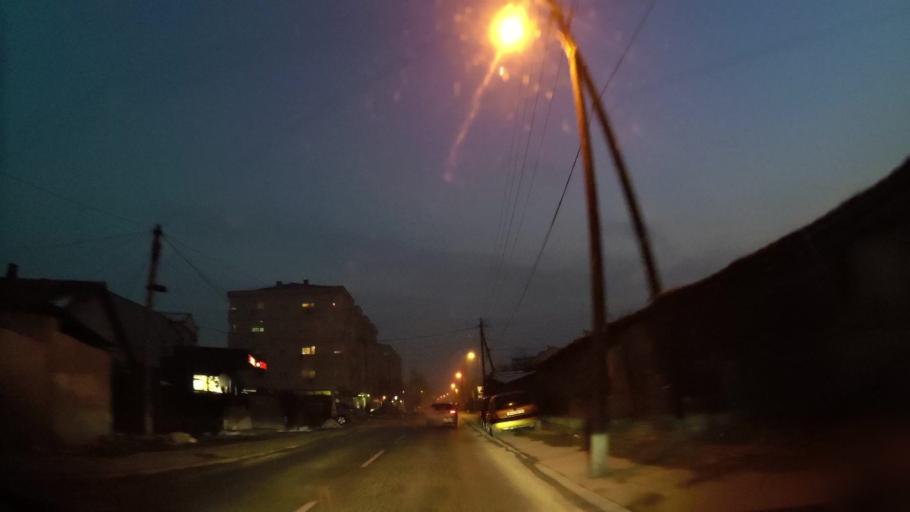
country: MK
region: Kisela Voda
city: Kisela Voda
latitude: 41.9973
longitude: 21.4999
